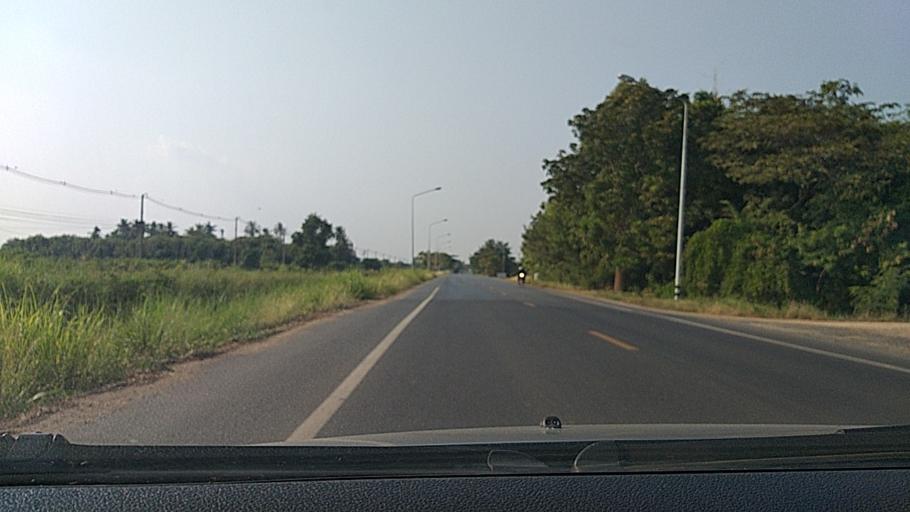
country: TH
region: Sing Buri
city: Phrom Buri
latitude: 14.8163
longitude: 100.4332
